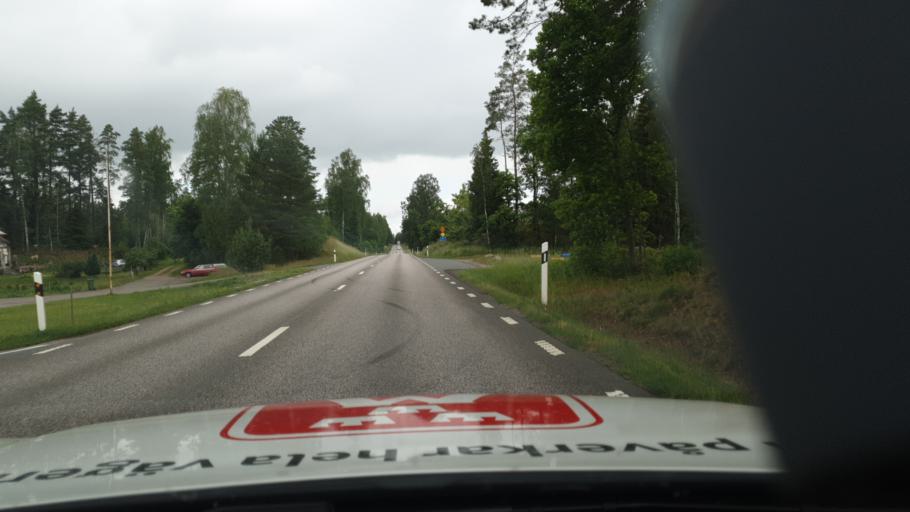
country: SE
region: Joenkoeping
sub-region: Mullsjo Kommun
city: Mullsjoe
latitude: 58.0567
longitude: 13.8052
